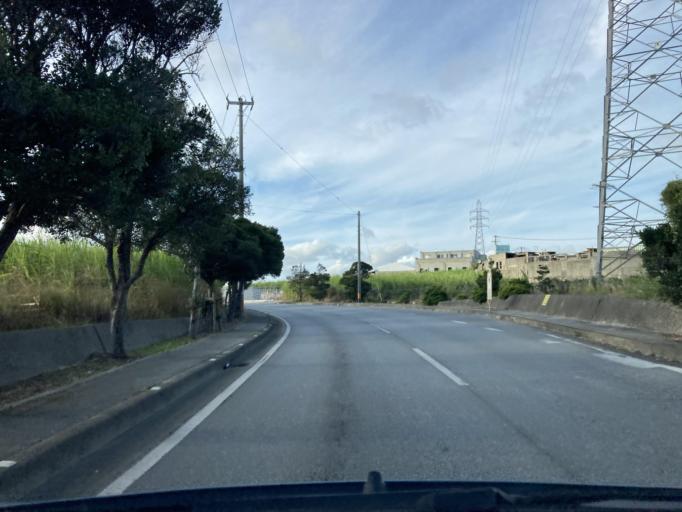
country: JP
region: Okinawa
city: Tomigusuku
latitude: 26.1567
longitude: 127.7398
